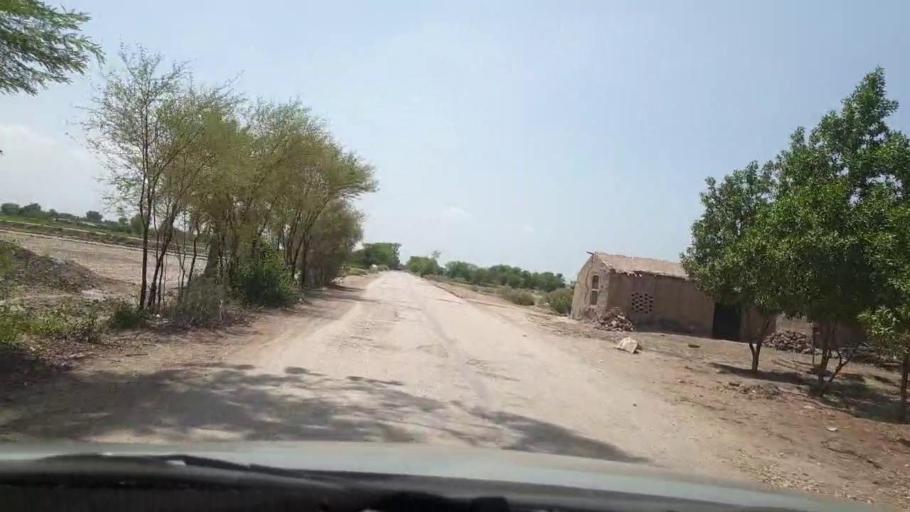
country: PK
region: Sindh
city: Pano Aqil
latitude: 27.6636
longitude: 69.1128
